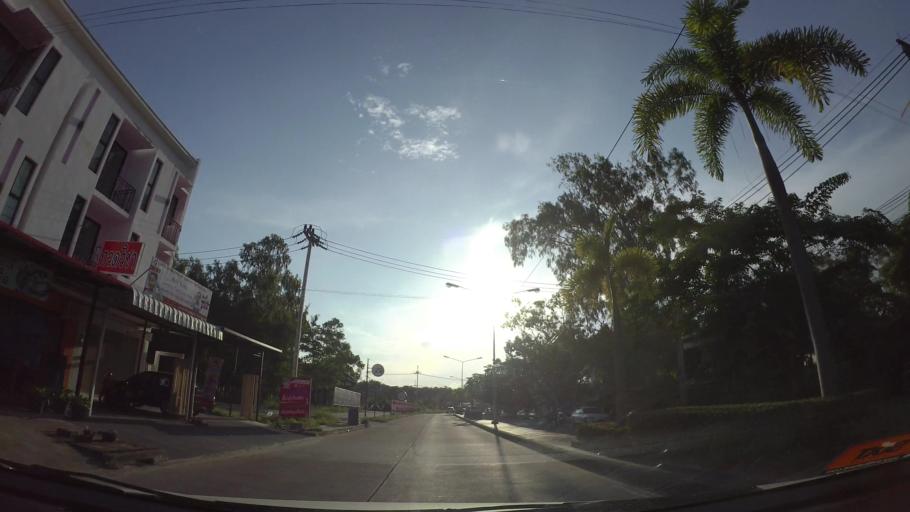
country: TH
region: Rayong
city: Rayong
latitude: 12.6858
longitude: 101.2834
